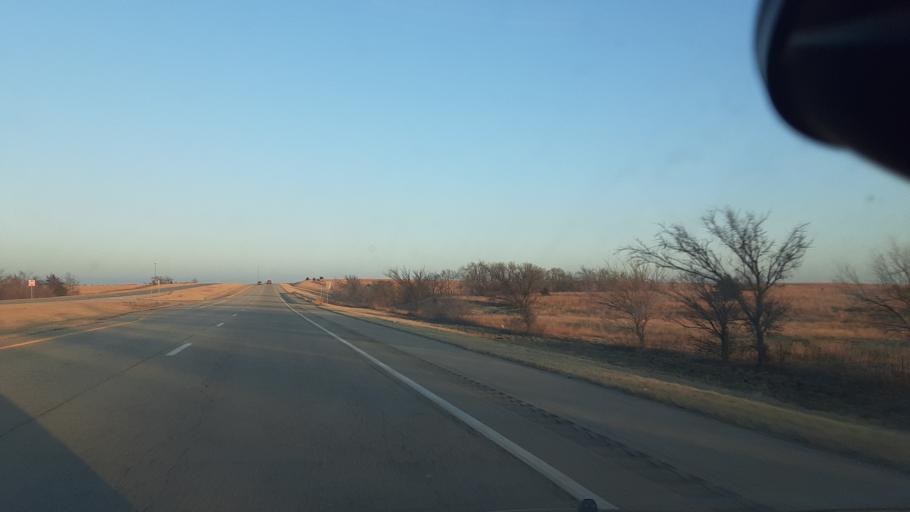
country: US
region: Oklahoma
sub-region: Noble County
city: Perry
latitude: 36.3980
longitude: -97.3647
